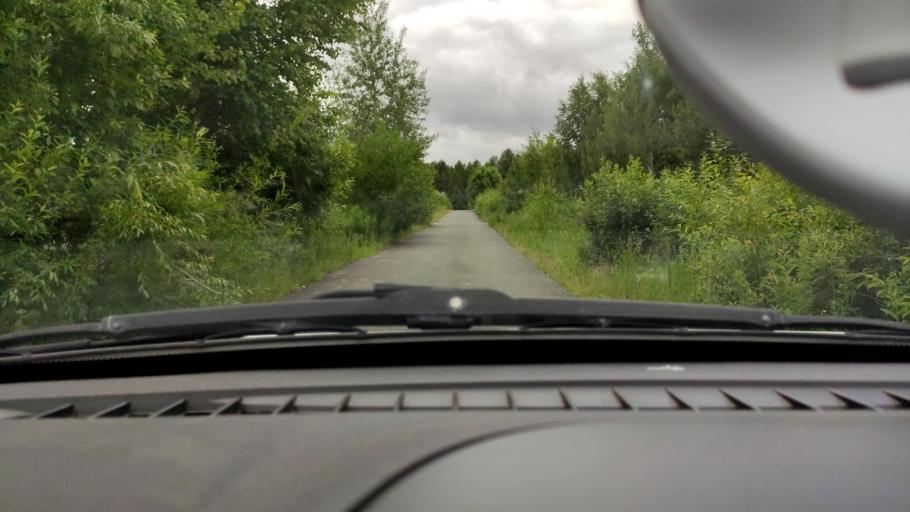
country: RU
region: Perm
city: Kondratovo
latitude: 58.0635
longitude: 56.1595
